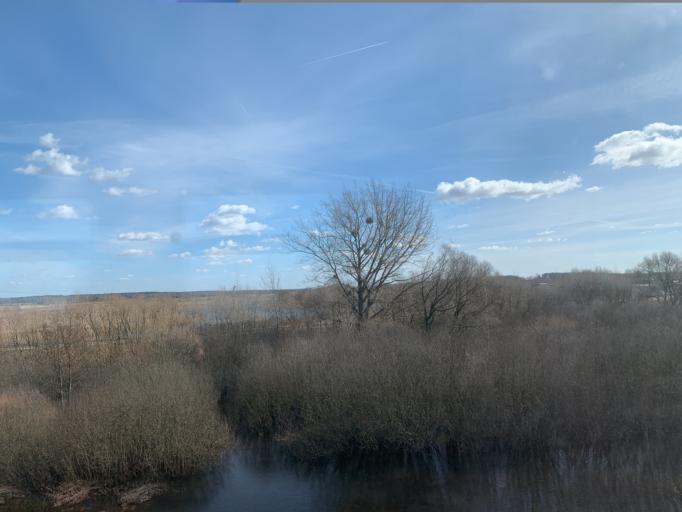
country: BY
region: Minsk
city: Novy Svyerzhan'
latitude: 53.4643
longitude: 26.7265
